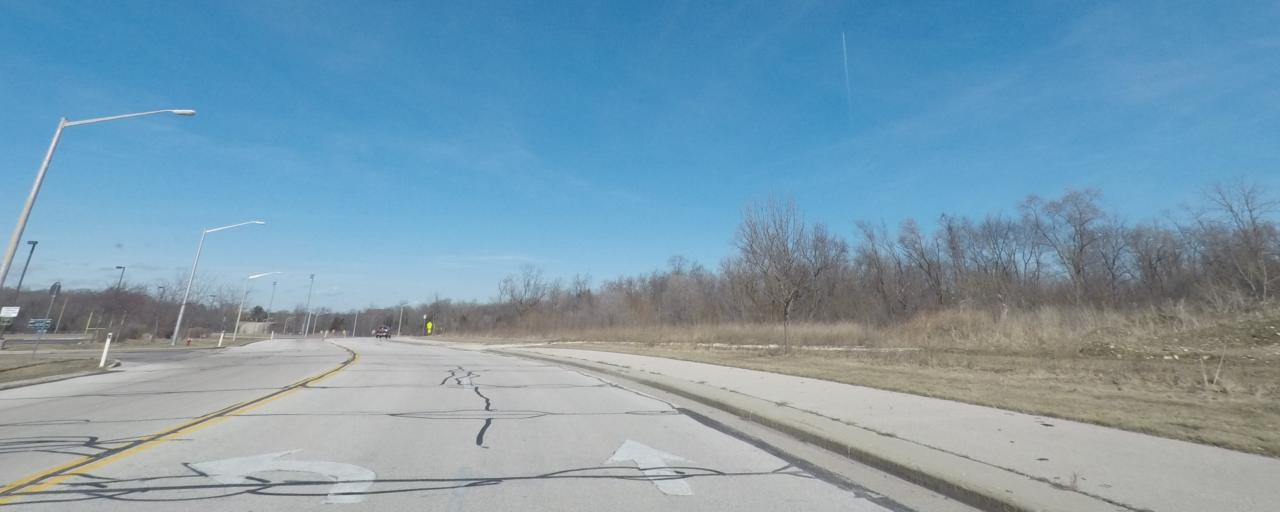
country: US
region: Wisconsin
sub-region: Waukesha County
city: Hartland
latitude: 43.1085
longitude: -88.3589
